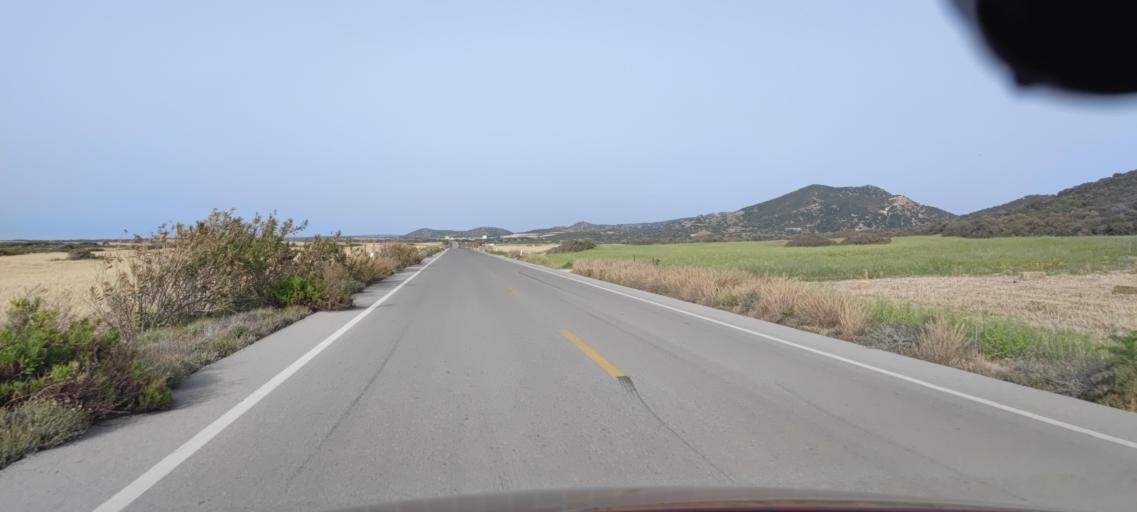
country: CY
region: Ammochostos
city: Leonarisso
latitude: 35.4742
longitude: 34.0490
